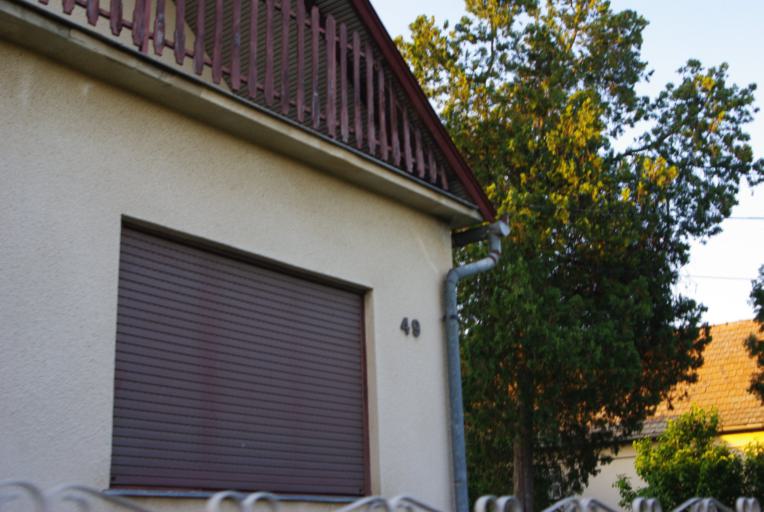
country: HU
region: Tolna
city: Bolcske
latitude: 46.7376
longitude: 18.9561
